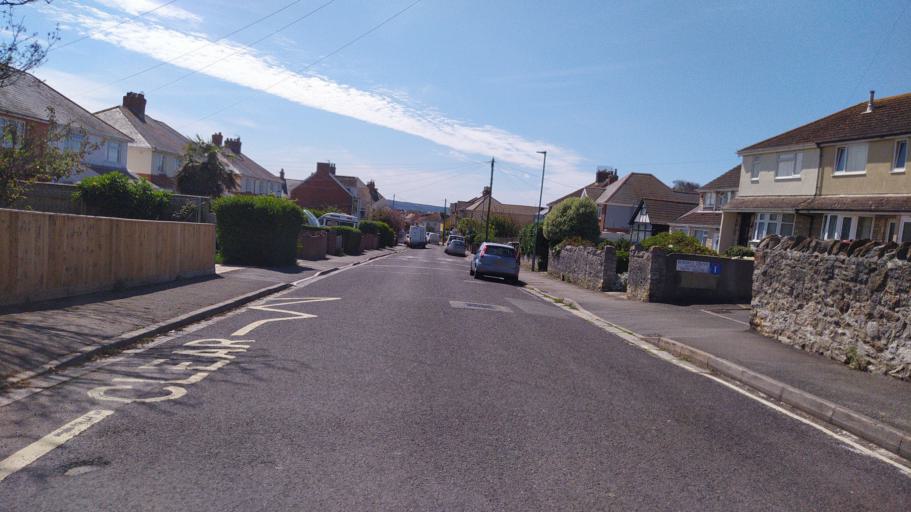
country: GB
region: England
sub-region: Dorset
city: Weymouth
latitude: 50.5941
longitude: -2.4782
